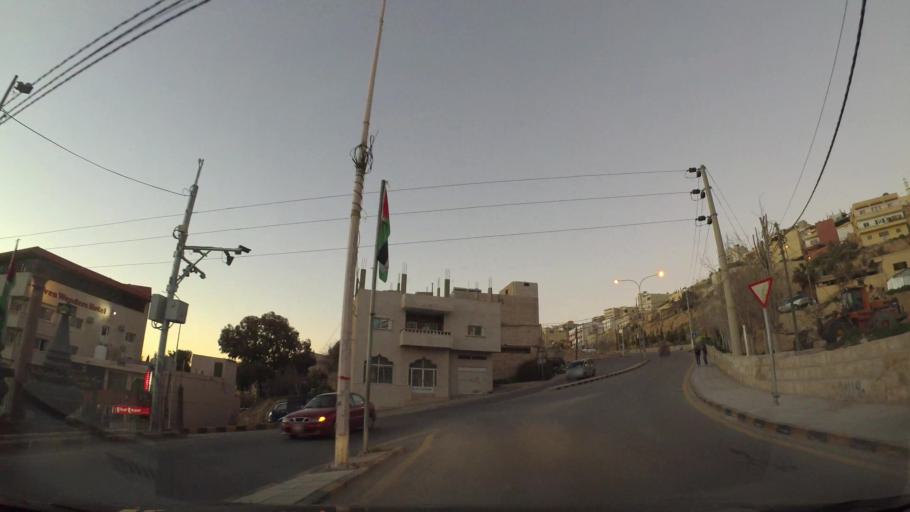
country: JO
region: Ma'an
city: Petra
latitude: 30.3181
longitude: 35.4824
